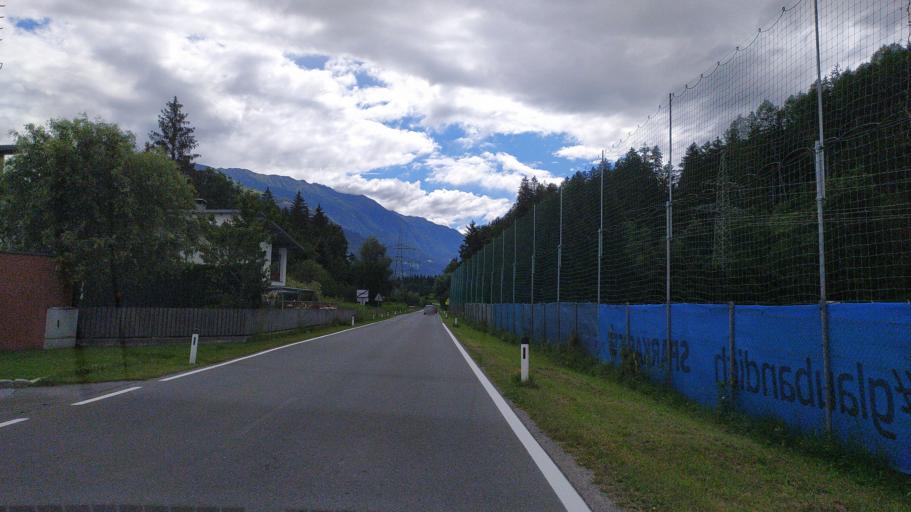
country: AT
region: Tyrol
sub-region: Politischer Bezirk Lienz
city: Tristach
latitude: 46.8149
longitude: 12.8015
